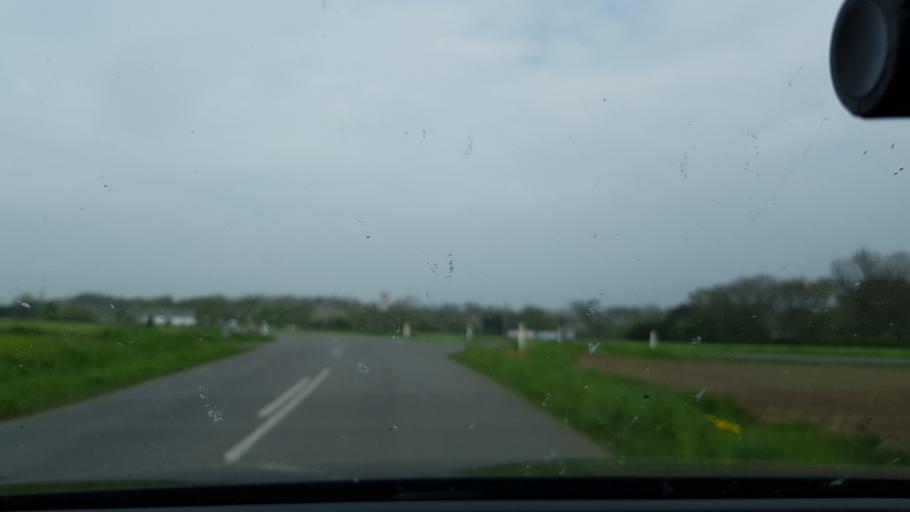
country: DK
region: Capital Region
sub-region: Bornholm Kommune
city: Nexo
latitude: 55.0223
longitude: 15.0972
